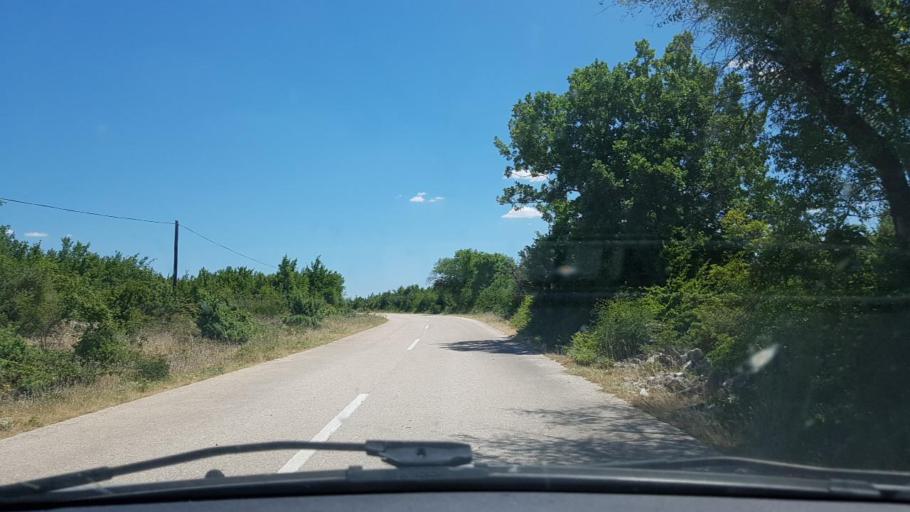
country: HR
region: Sibensko-Kniniska
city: Kistanje
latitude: 43.9704
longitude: 15.9746
